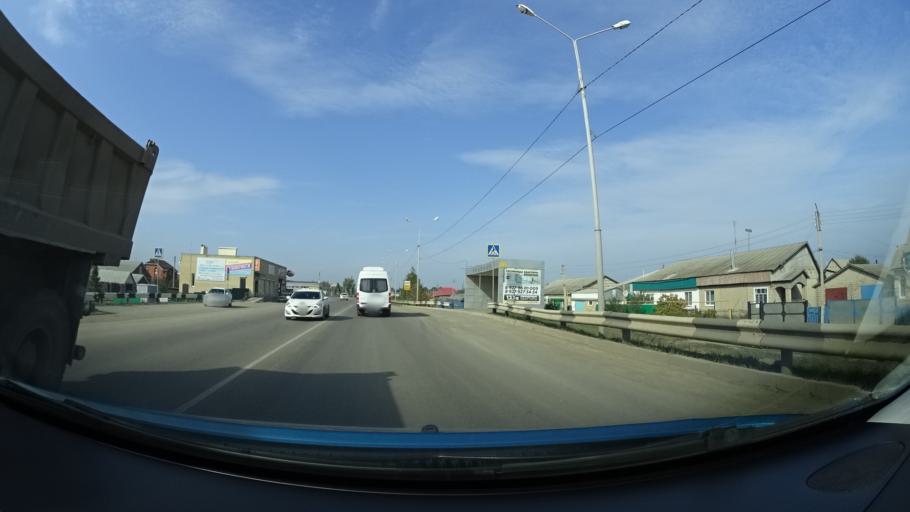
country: RU
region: Bashkortostan
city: Tuymazy
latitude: 54.5922
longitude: 53.7420
